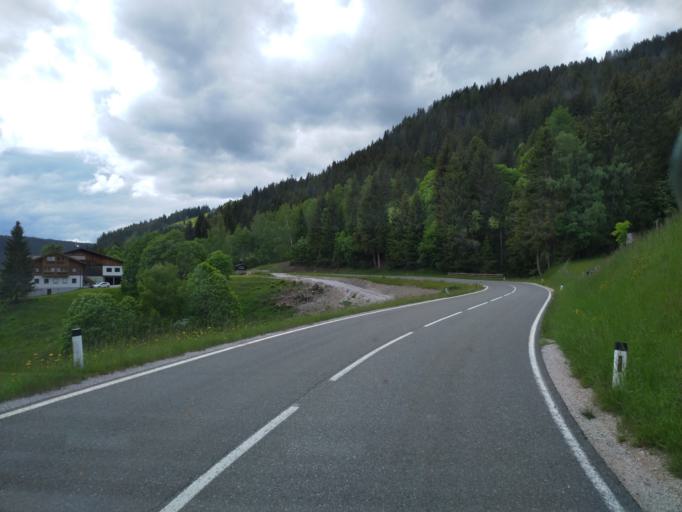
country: AT
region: Salzburg
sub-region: Politischer Bezirk Sankt Johann im Pongau
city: Filzmoos
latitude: 47.4359
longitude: 13.5730
